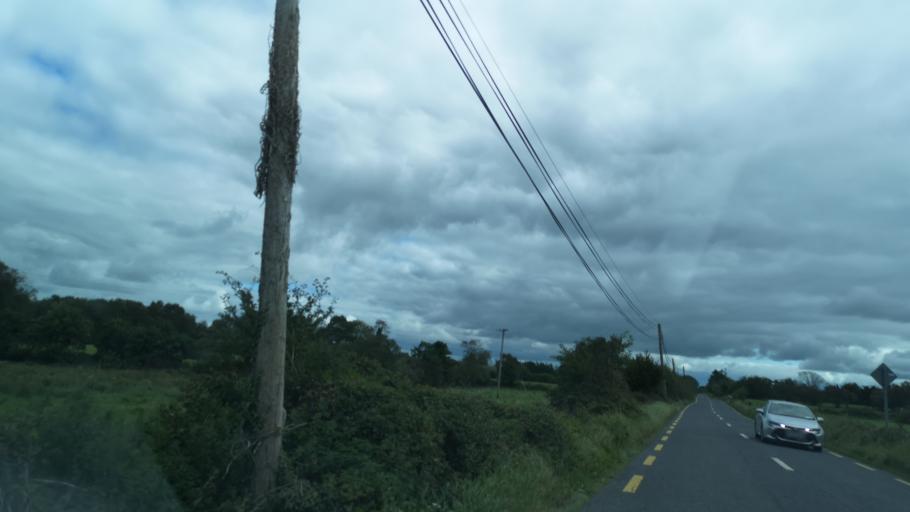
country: IE
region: Connaught
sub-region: County Galway
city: Ballinasloe
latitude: 53.3116
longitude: -8.1602
